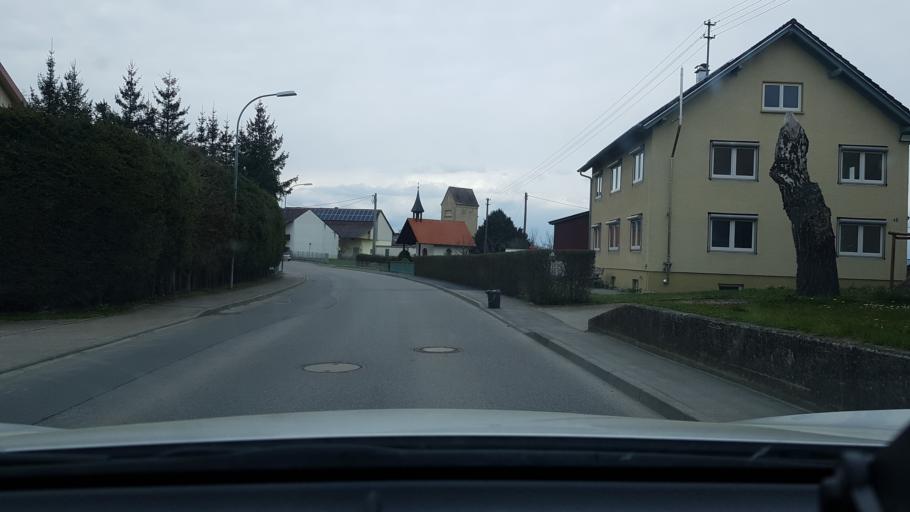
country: DE
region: Baden-Wuerttemberg
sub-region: Tuebingen Region
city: Oberstadion
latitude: 48.1816
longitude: 9.7050
